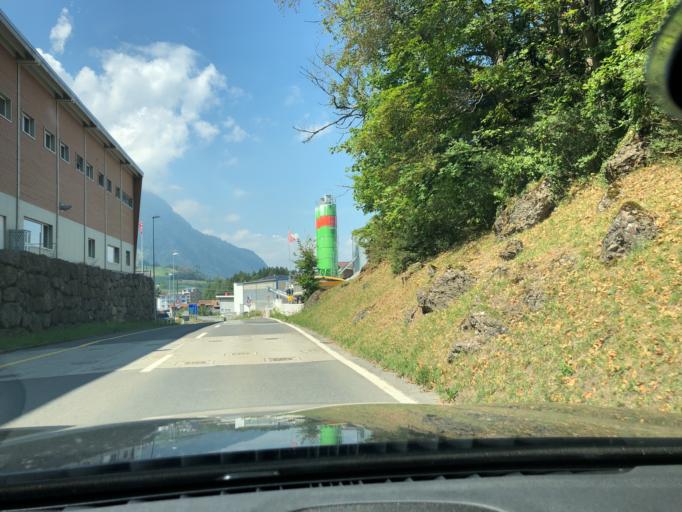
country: CH
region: Schwyz
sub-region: Bezirk Schwyz
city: Goldau
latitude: 47.0411
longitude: 8.5566
